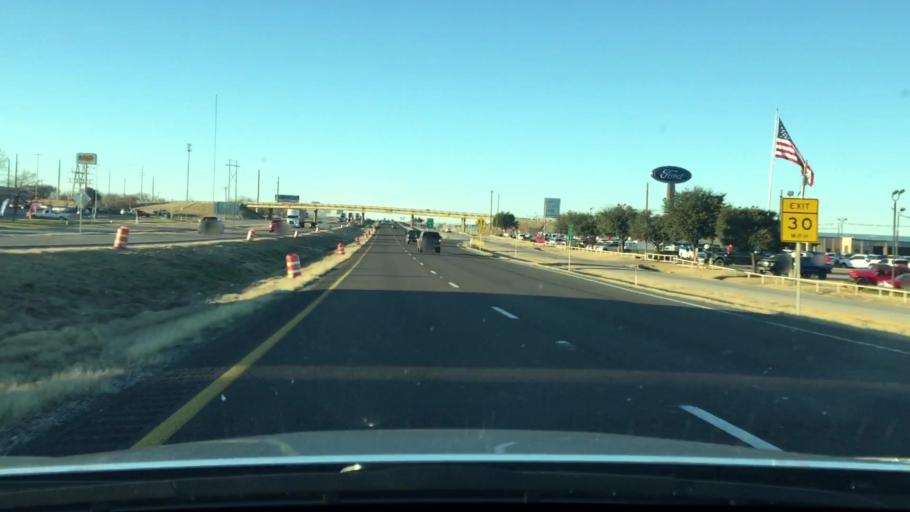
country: US
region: Texas
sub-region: Cooke County
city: Gainesville
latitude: 33.6787
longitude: -97.1546
